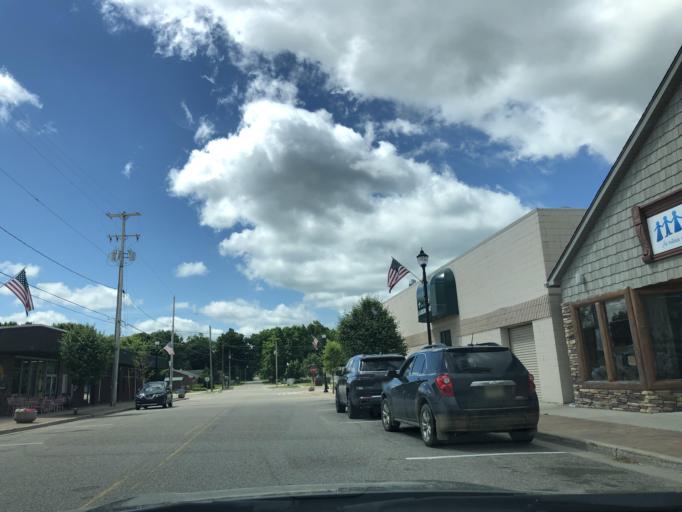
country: US
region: Michigan
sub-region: Clare County
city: Harrison
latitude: 44.0205
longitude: -84.8012
